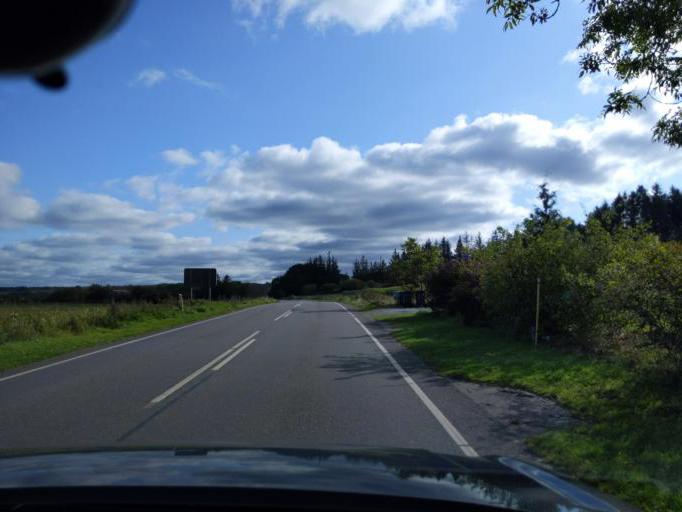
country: DK
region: North Denmark
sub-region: Mariagerfjord Kommune
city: Hobro
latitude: 56.5587
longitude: 9.7243
